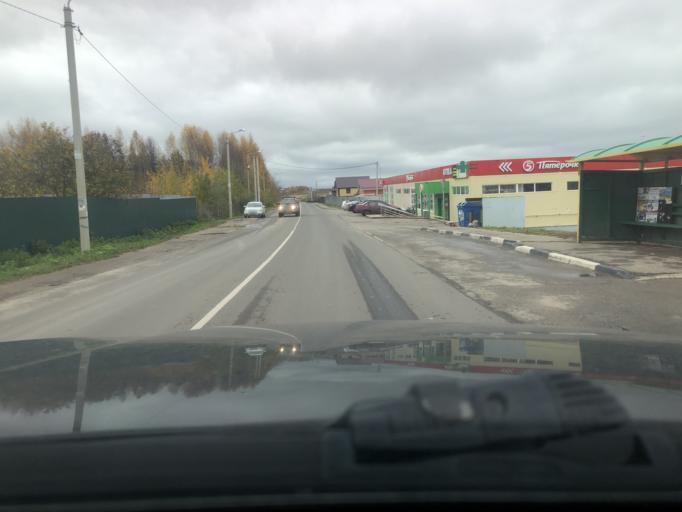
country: RU
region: Moskovskaya
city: Sergiyev Posad
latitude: 56.3073
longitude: 38.1011
